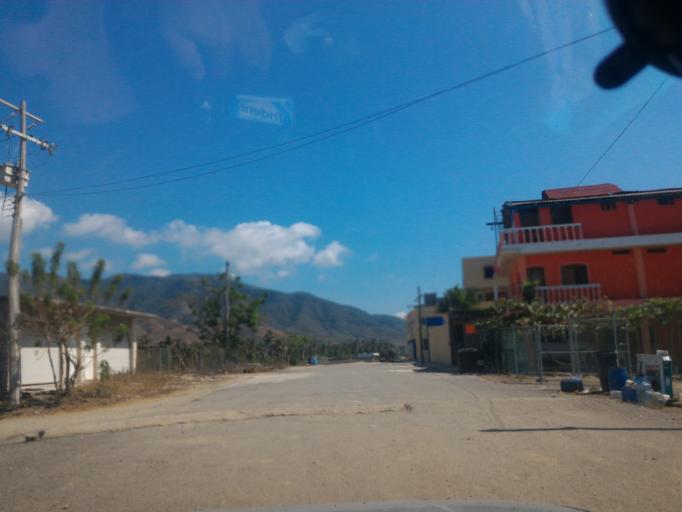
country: MX
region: Michoacan
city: Coahuayana Viejo
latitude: 18.5886
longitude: -103.6829
